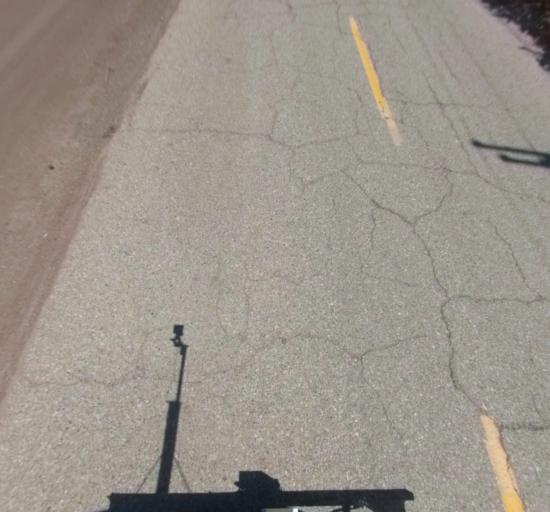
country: US
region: California
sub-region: Madera County
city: Chowchilla
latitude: 37.0282
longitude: -120.3106
